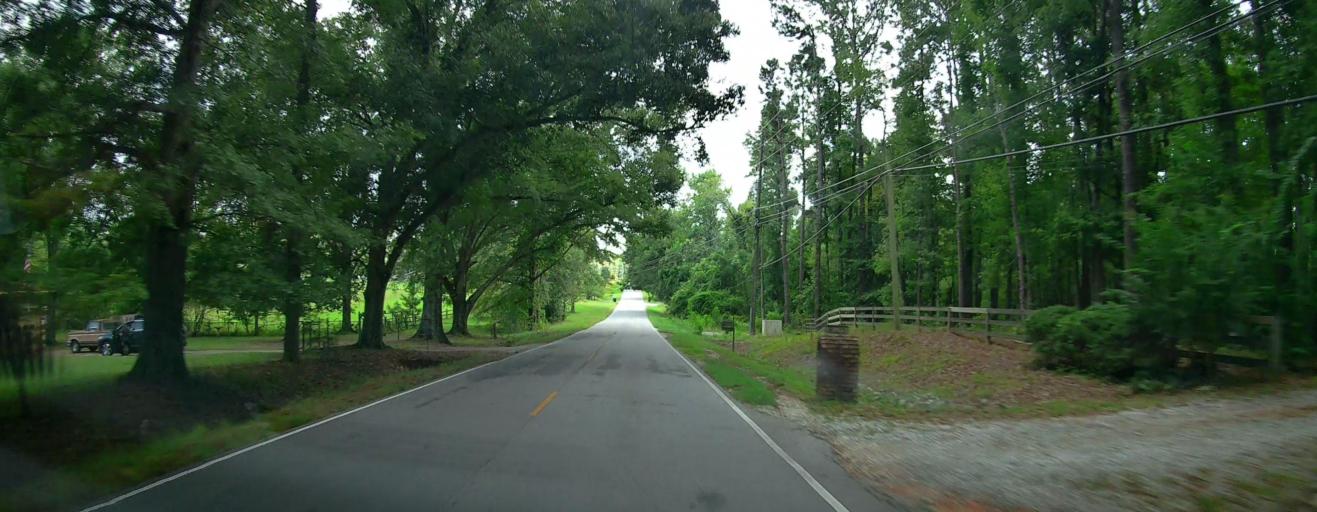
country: US
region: Alabama
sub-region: Russell County
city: Phenix City
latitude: 32.5926
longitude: -84.9785
